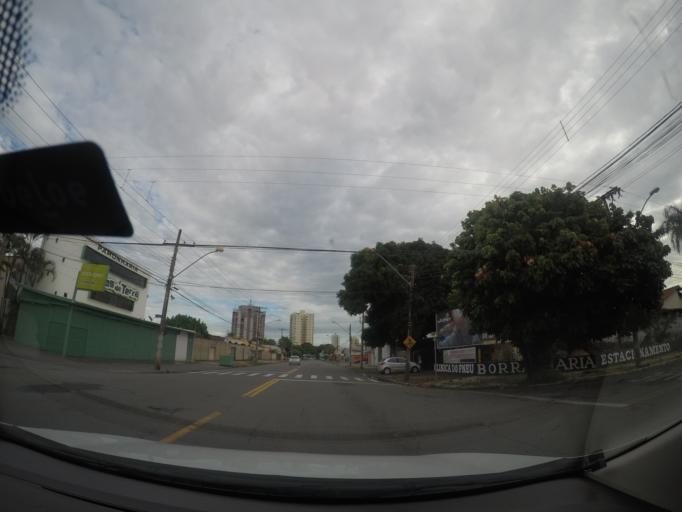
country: BR
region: Goias
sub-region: Goiania
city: Goiania
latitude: -16.6815
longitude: -49.2776
